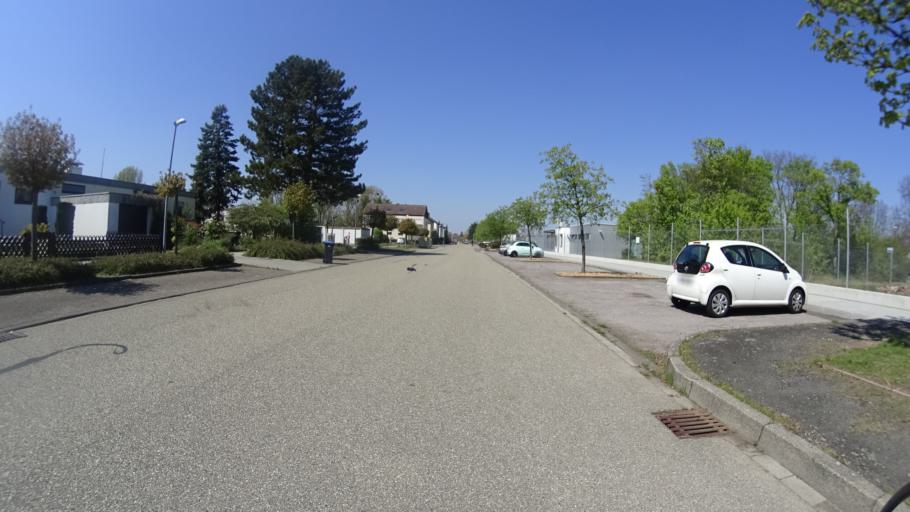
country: DE
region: Baden-Wuerttemberg
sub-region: Karlsruhe Region
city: Karlsruhe
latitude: 49.0418
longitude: 8.3993
